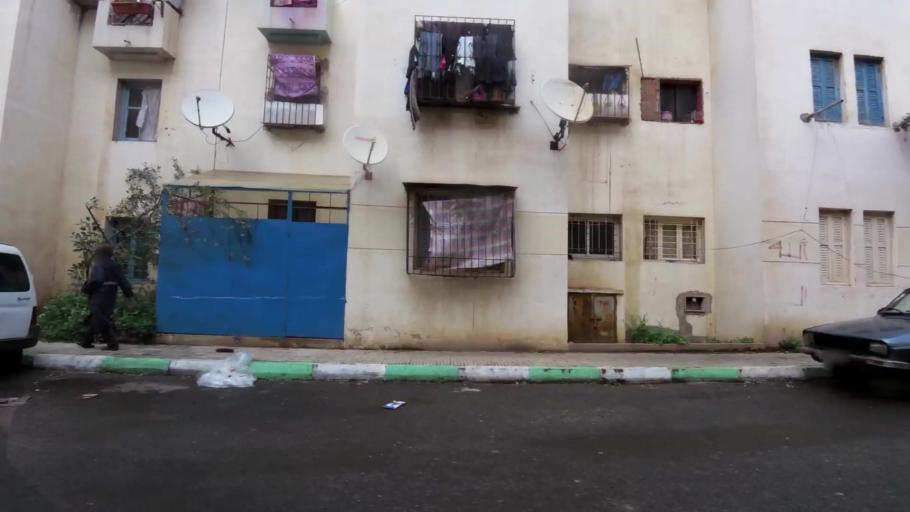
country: MA
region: Grand Casablanca
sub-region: Casablanca
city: Casablanca
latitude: 33.5330
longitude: -7.6497
